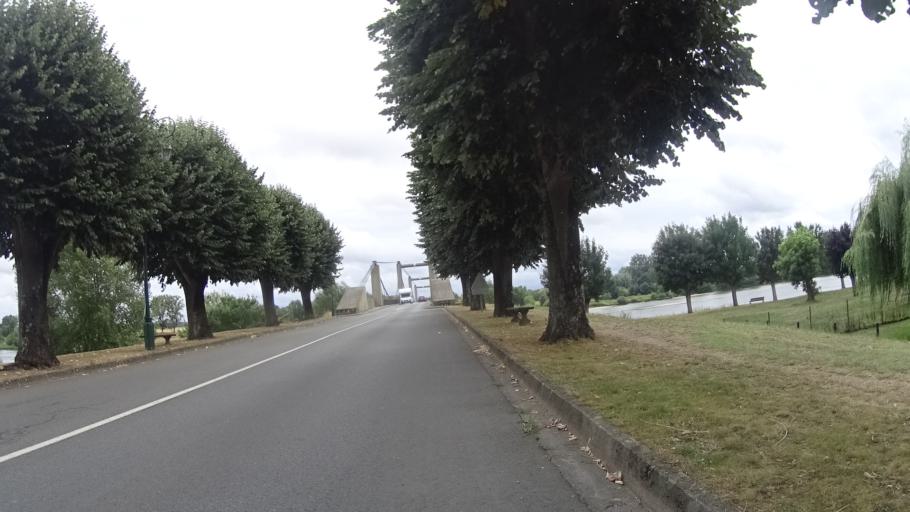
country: FR
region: Centre
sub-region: Departement du Loiret
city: Meung-sur-Loire
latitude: 47.8239
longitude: 1.6997
